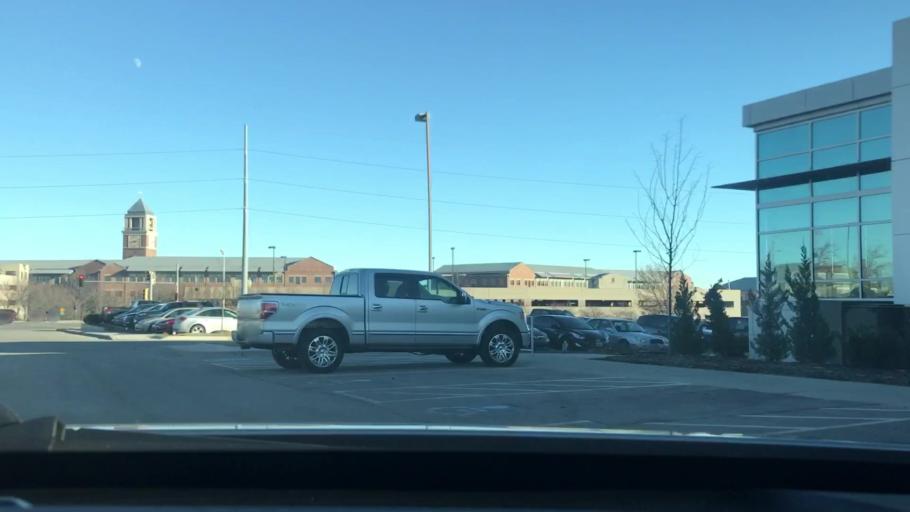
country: US
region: Kansas
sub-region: Johnson County
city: Overland Park
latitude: 38.9193
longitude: -94.6620
